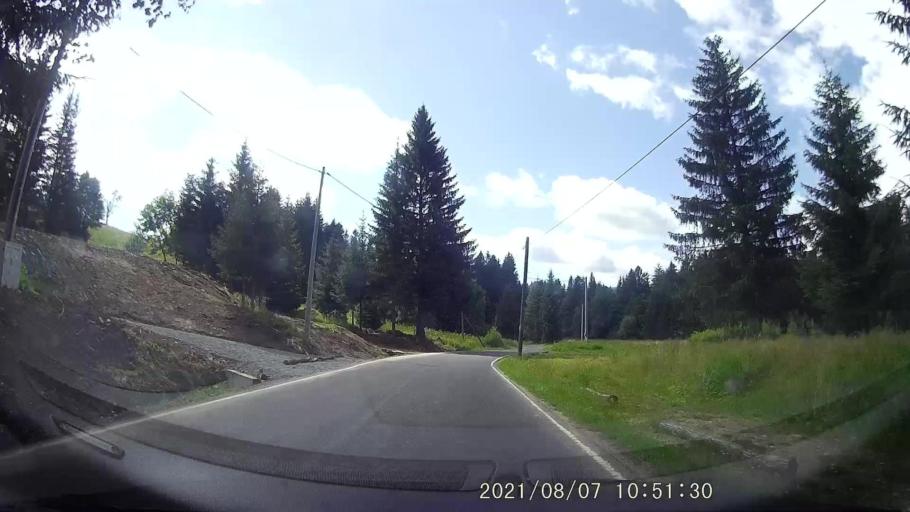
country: PL
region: Lower Silesian Voivodeship
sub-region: Powiat klodzki
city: Polanica-Zdroj
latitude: 50.2886
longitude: 16.4683
